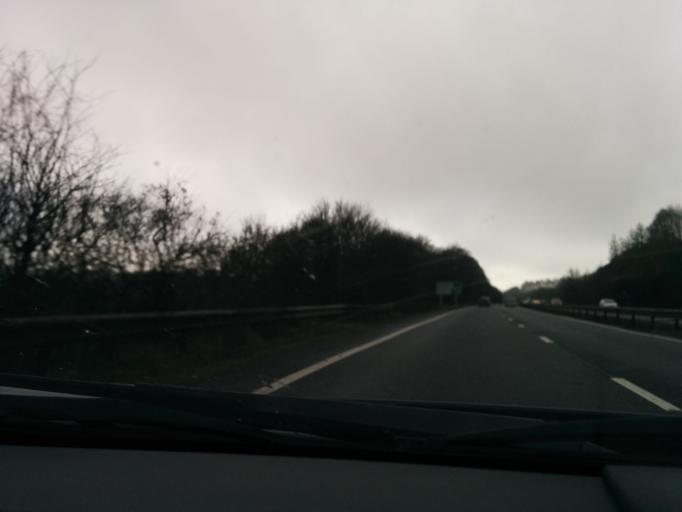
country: GB
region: England
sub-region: Hampshire
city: Highclere
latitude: 51.2882
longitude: -1.3386
